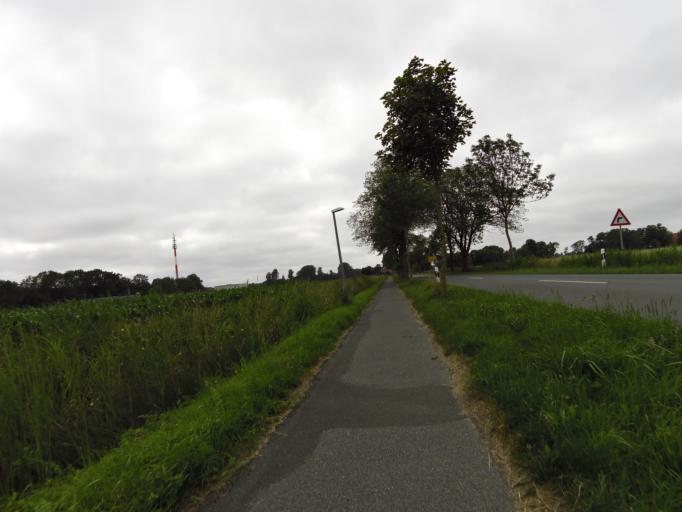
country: DE
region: Lower Saxony
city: Padingbuttel
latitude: 53.7223
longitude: 8.5422
